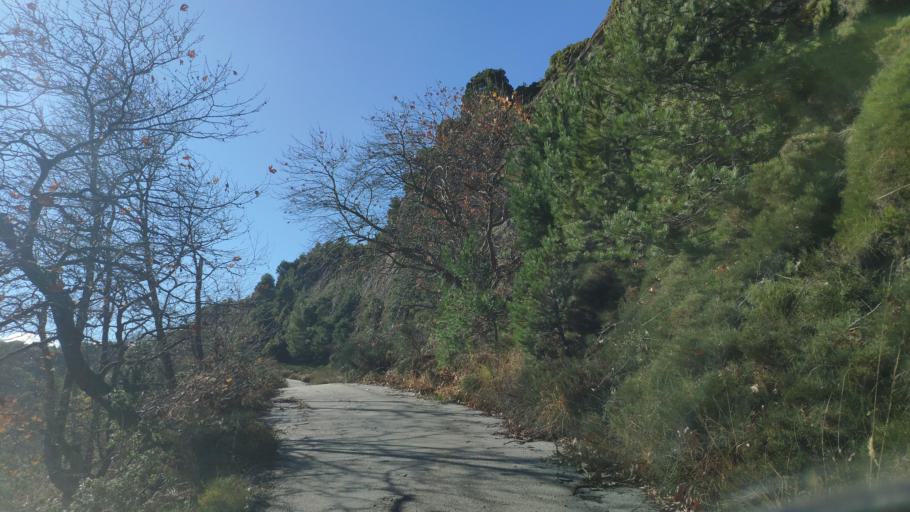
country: GR
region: West Greece
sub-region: Nomos Achaias
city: Aiyira
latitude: 38.0590
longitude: 22.4565
